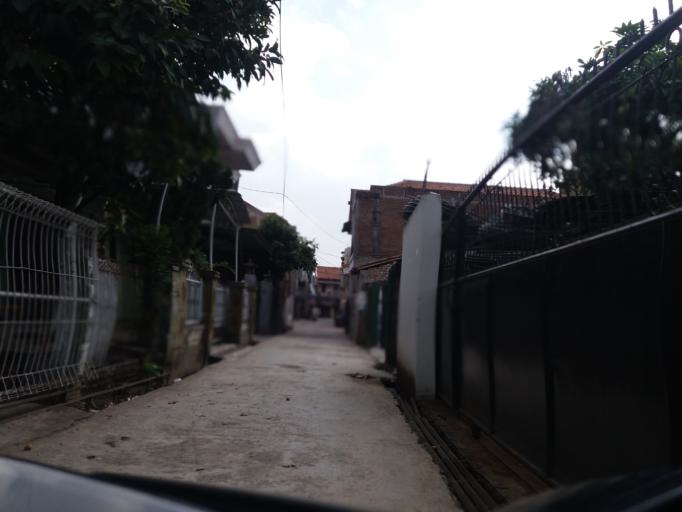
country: ID
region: West Java
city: Bandung
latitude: -6.9243
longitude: 107.6584
